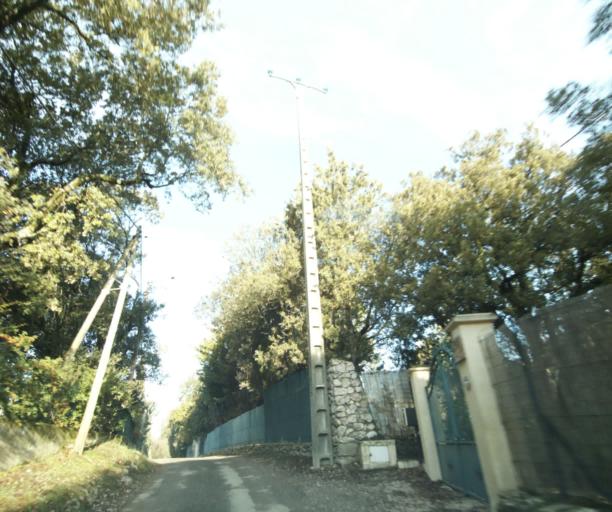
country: FR
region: Provence-Alpes-Cote d'Azur
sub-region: Departement du Var
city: Tourves
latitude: 43.3981
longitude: 5.9327
